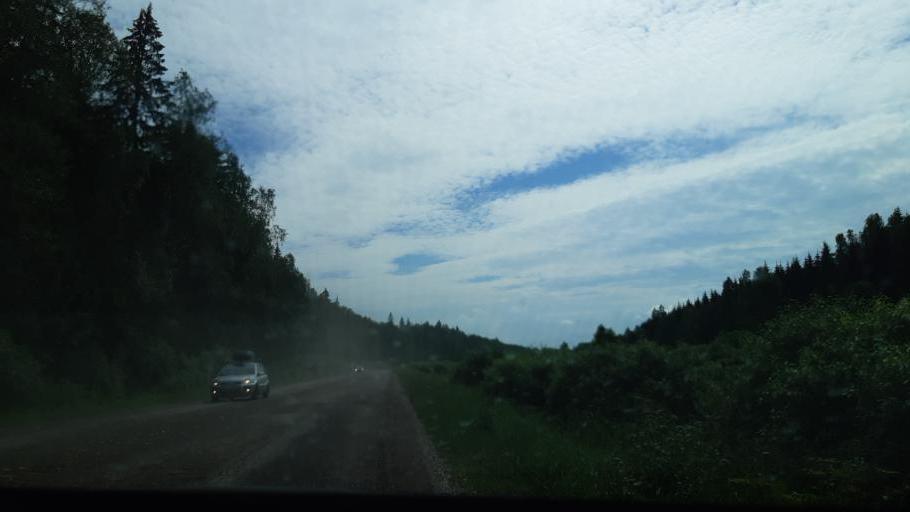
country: RU
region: Moskovskaya
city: Vereya
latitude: 55.2802
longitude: 36.0832
